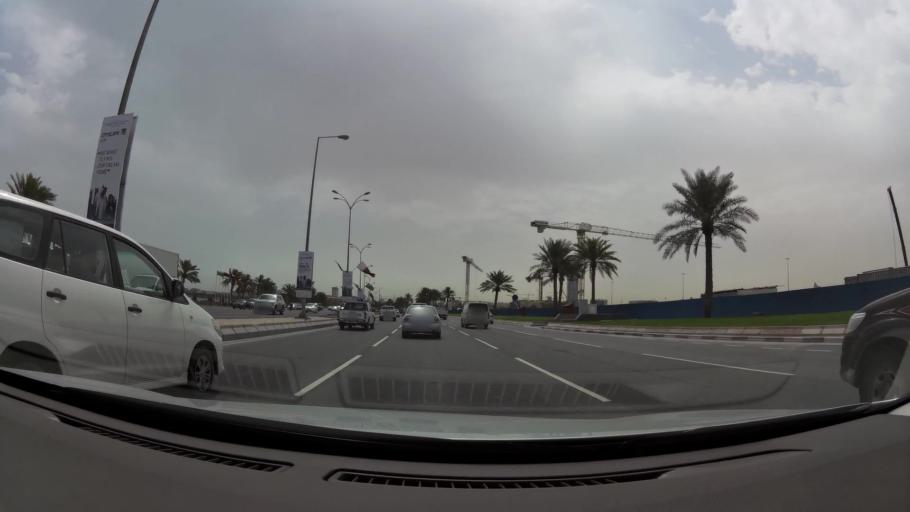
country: QA
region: Baladiyat ad Dawhah
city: Doha
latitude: 25.3013
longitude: 51.5182
